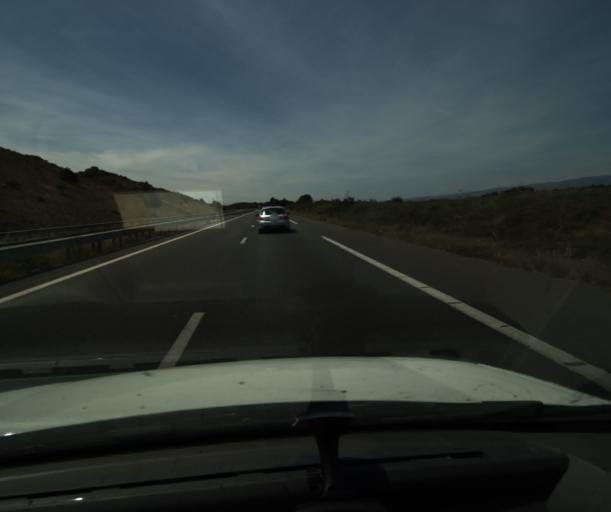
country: FR
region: Languedoc-Roussillon
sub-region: Departement de l'Aude
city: Fabrezan
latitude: 43.1734
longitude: 2.6709
